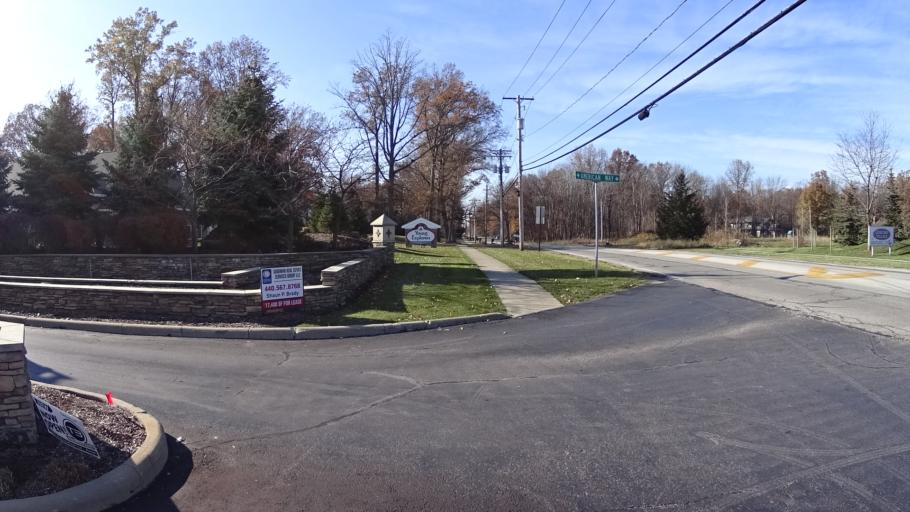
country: US
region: Ohio
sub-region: Lorain County
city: Avon Center
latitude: 41.4670
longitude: -82.0272
